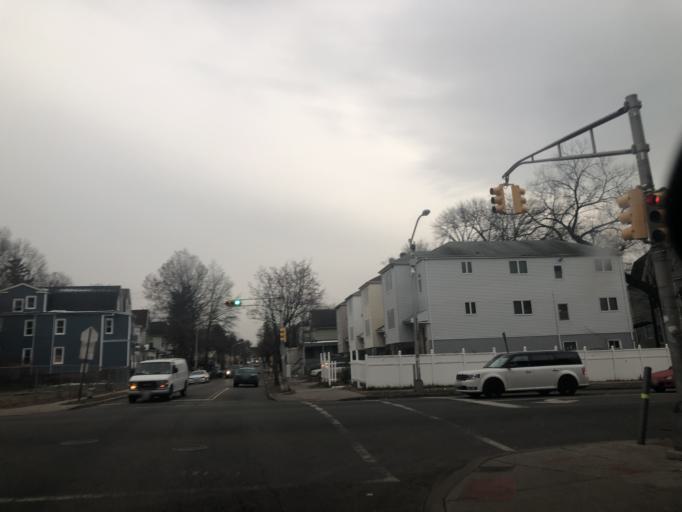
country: US
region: New Jersey
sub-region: Essex County
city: East Orange
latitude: 40.7692
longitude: -74.2095
